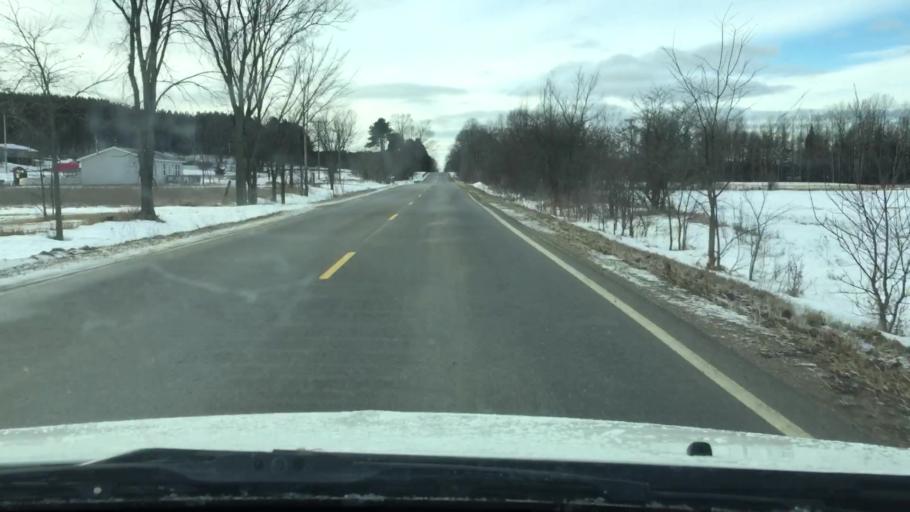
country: US
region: Michigan
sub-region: Wexford County
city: Manton
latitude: 44.4036
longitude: -85.4248
